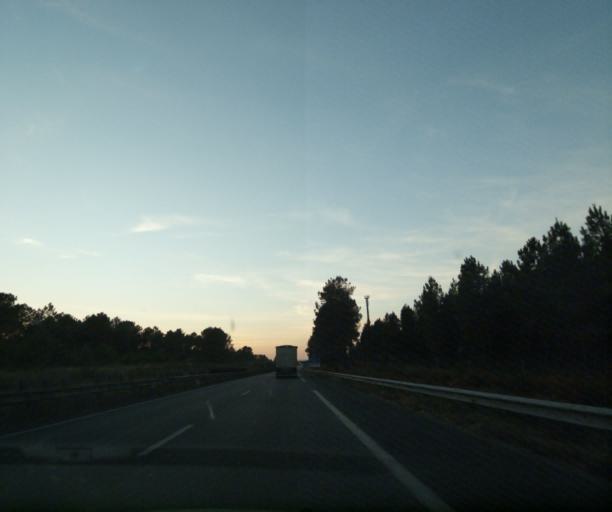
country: FR
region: Aquitaine
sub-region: Departement de la Gironde
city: Portets
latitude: 44.6390
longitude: -0.4257
